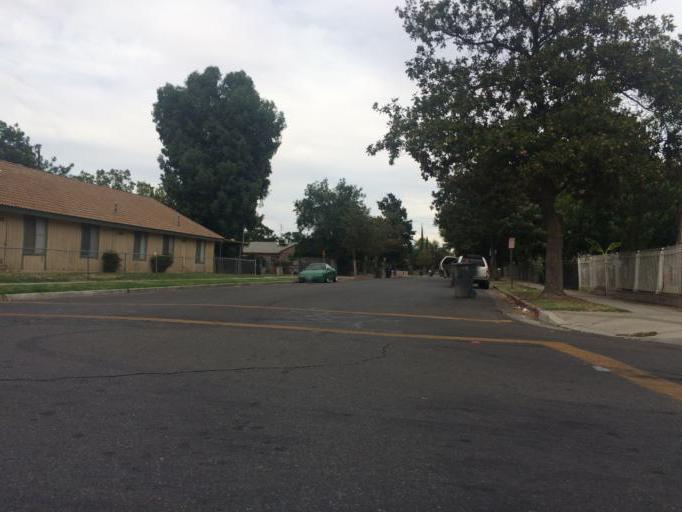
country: US
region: California
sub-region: Fresno County
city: Fresno
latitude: 36.7394
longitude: -119.7501
